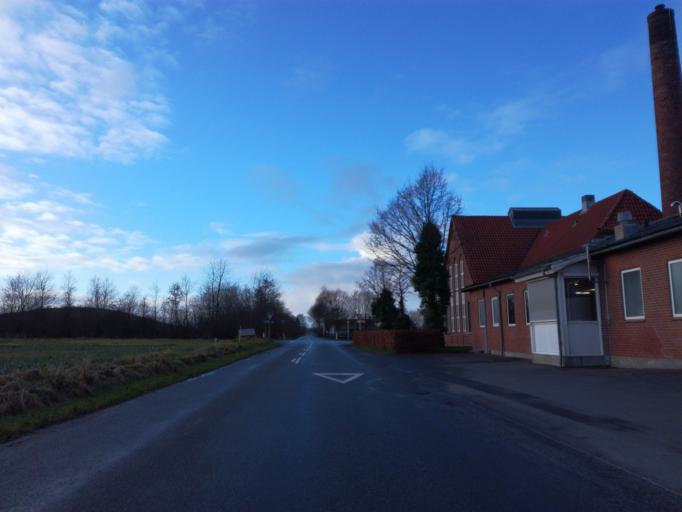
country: DK
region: South Denmark
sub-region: Fredericia Kommune
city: Taulov
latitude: 55.5680
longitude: 9.6064
